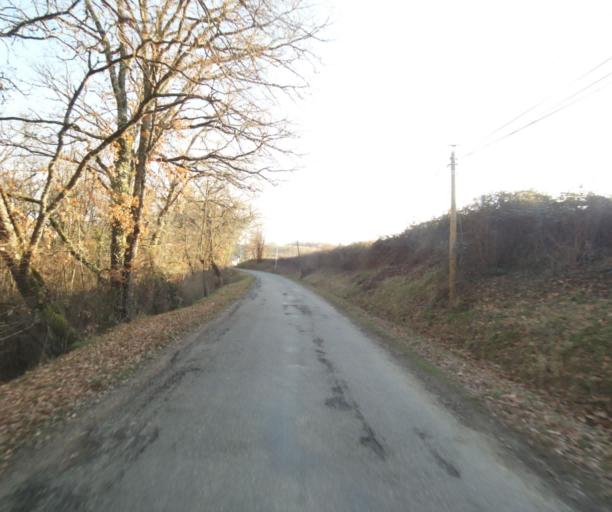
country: FR
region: Midi-Pyrenees
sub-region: Departement du Tarn-et-Garonne
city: Moissac
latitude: 44.1334
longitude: 1.1372
